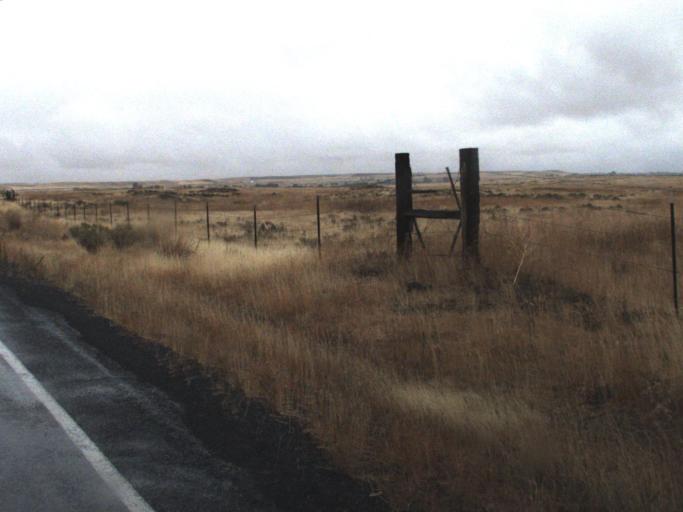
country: US
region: Washington
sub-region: Lincoln County
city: Davenport
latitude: 47.3335
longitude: -117.9834
